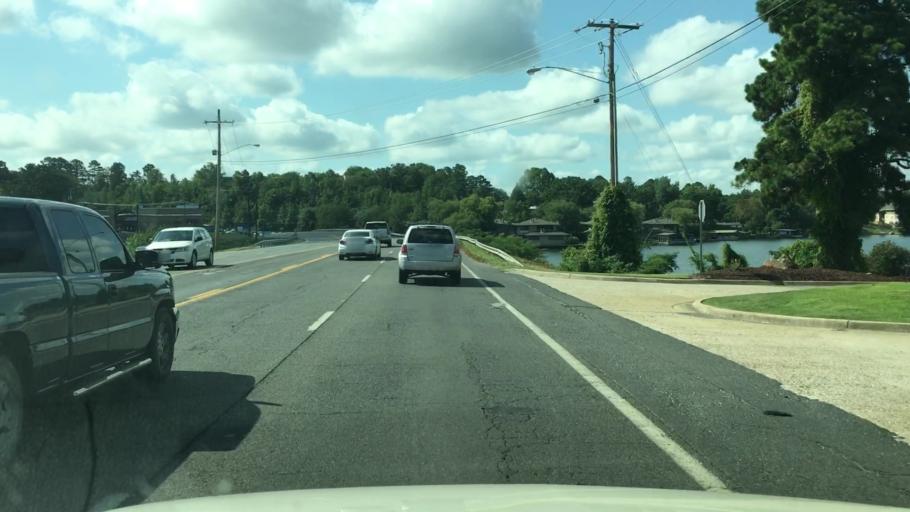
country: US
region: Arkansas
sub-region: Garland County
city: Piney
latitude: 34.4979
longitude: -93.1220
